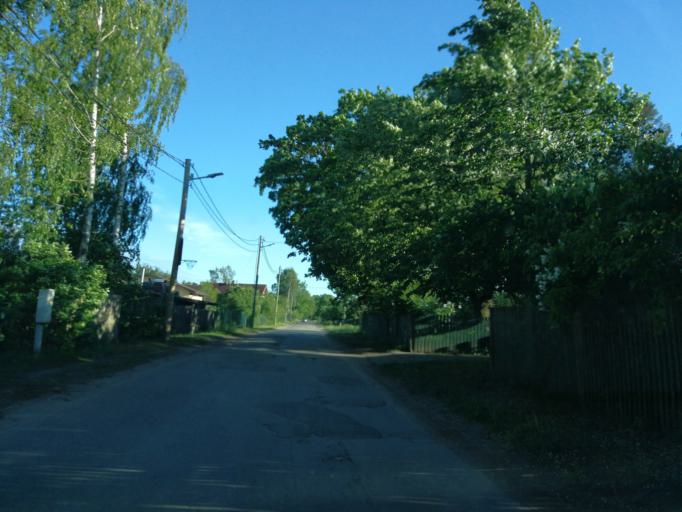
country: LV
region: Riga
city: Jaunciems
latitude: 57.0582
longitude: 24.1385
